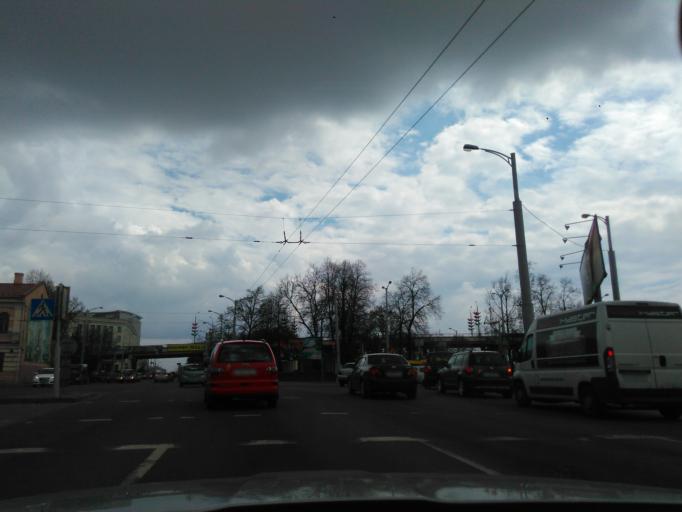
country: BY
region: Minsk
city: Minsk
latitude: 53.8934
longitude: 27.5408
